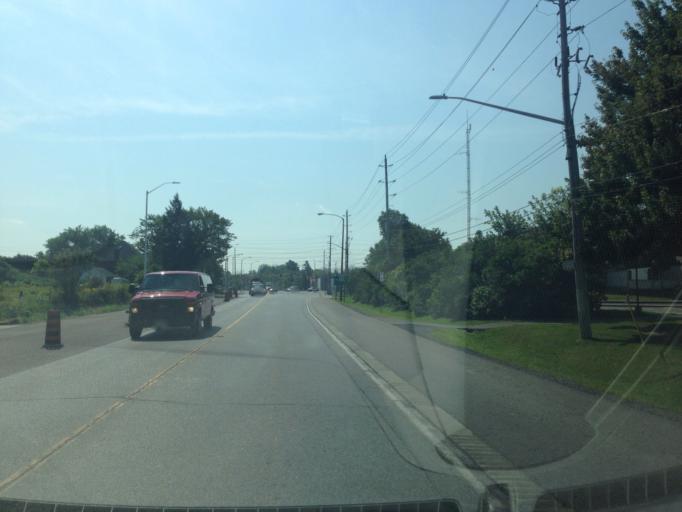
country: CA
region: Ontario
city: Ottawa
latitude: 45.4215
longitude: -75.5969
